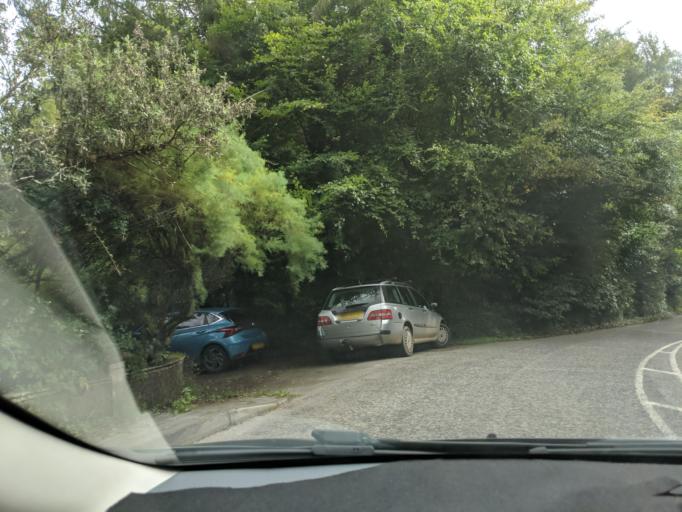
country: GB
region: England
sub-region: Cornwall
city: Par
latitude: 50.3588
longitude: -4.7055
